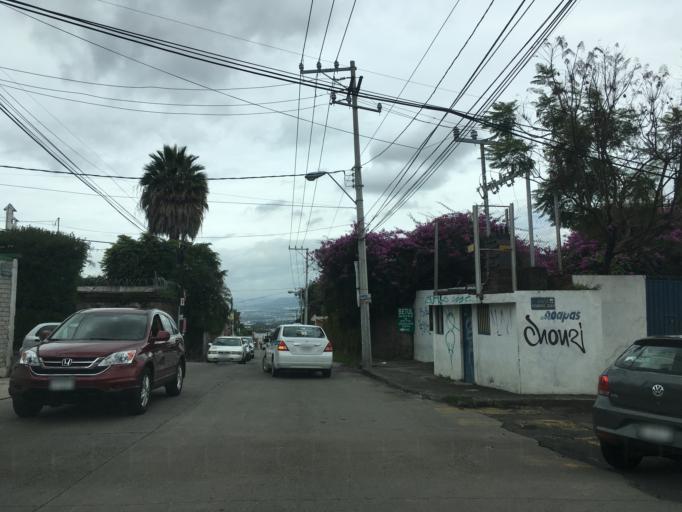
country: MX
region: Michoacan
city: Morelia
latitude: 19.6768
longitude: -101.1903
